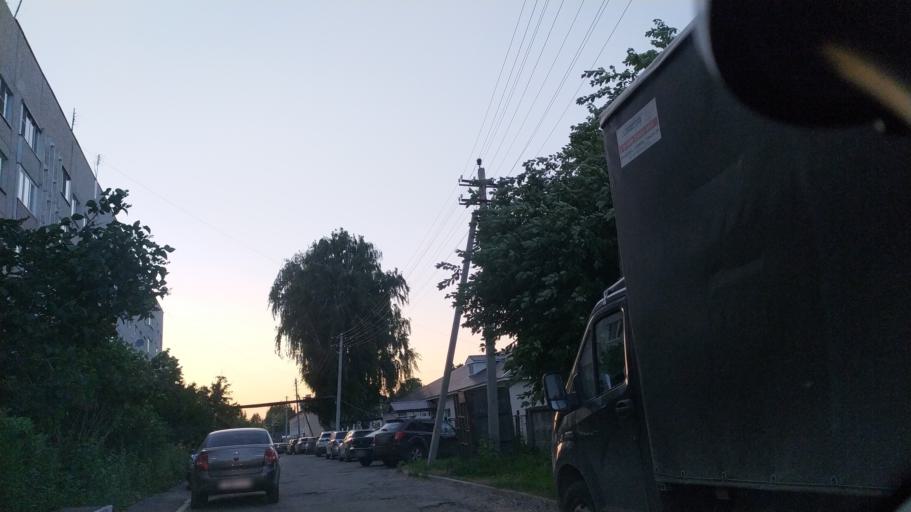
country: RU
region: Chuvashia
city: Ishley
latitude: 56.1256
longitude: 47.0428
